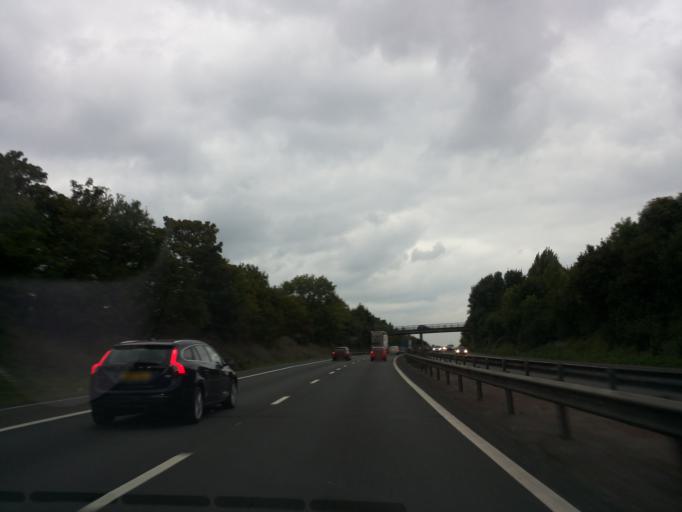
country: GB
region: England
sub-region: Kent
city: Faversham
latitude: 51.3023
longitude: 0.8742
